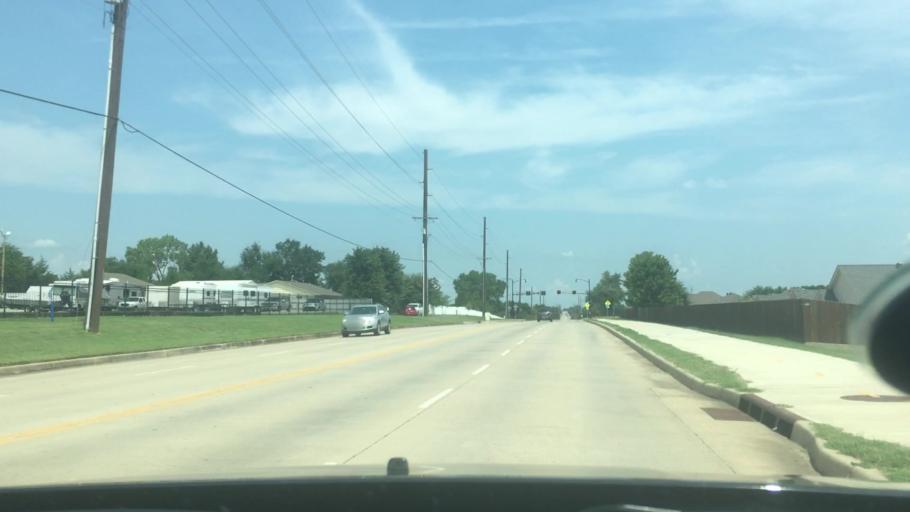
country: US
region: Oklahoma
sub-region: Pottawatomie County
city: Shawnee
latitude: 35.3347
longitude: -96.8943
